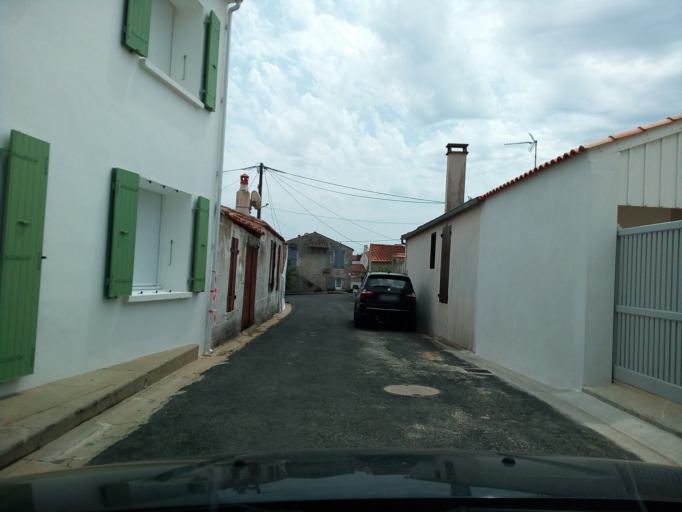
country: FR
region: Poitou-Charentes
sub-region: Departement de la Charente-Maritime
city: Dolus-d'Oleron
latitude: 45.9178
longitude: -1.3341
